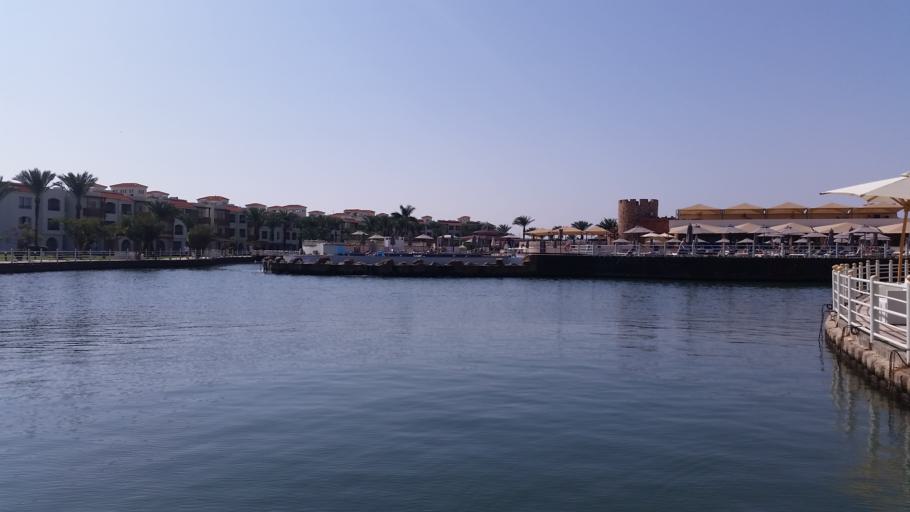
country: EG
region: Red Sea
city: Makadi Bay
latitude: 27.0999
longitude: 33.8341
